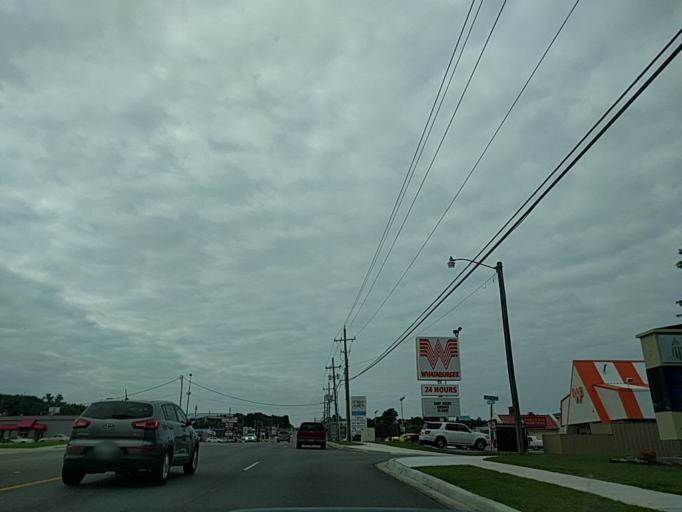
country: US
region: Oklahoma
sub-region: Tulsa County
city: Jenks
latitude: 36.0784
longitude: -95.9044
